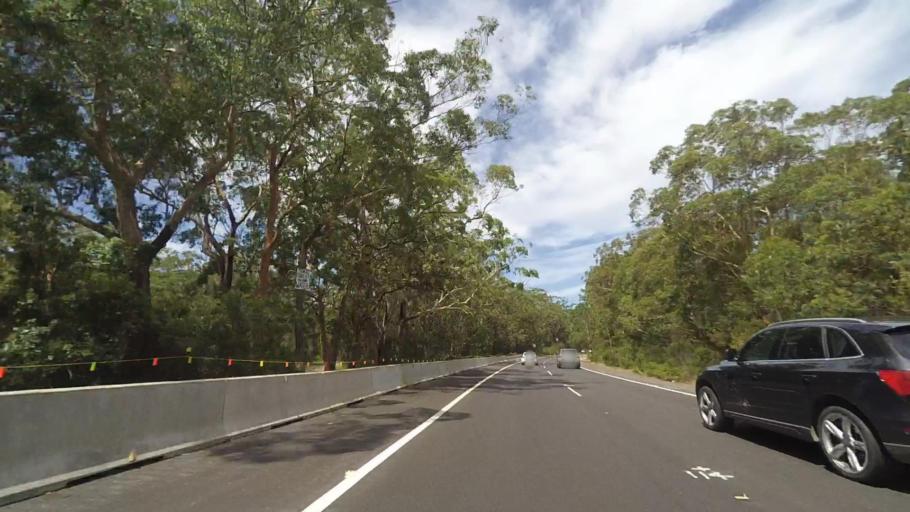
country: AU
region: New South Wales
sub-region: Port Stephens Shire
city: Anna Bay
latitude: -32.7795
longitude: 151.9899
